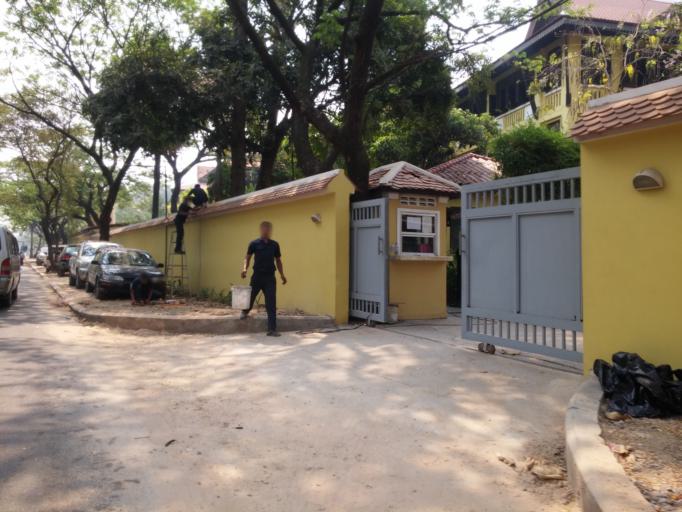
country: KH
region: Siem Reap
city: Siem Reap
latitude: 13.3643
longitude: 103.8570
